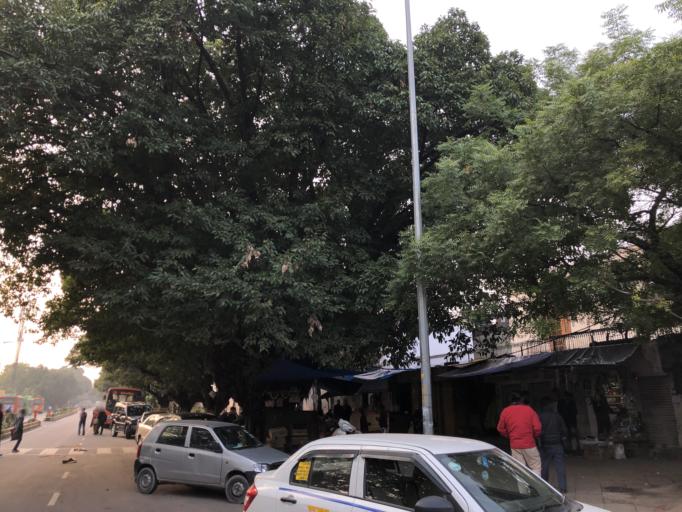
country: IN
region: NCT
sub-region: New Delhi
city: New Delhi
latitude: 28.6174
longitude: 77.2046
